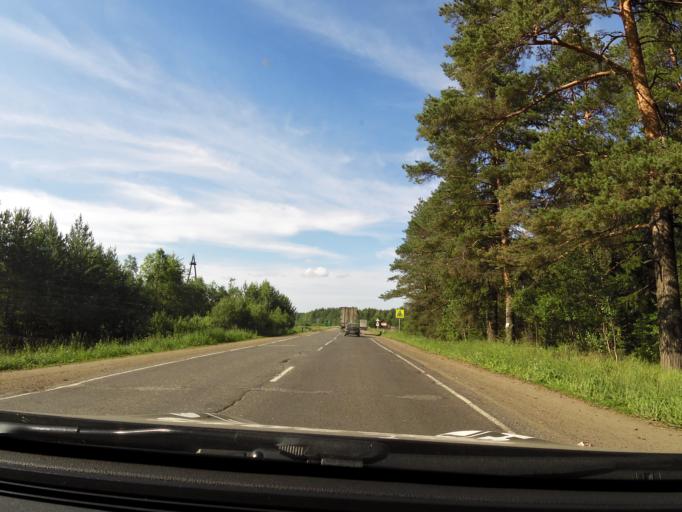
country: RU
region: Kirov
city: Belaya Kholunitsa
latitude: 58.8662
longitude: 50.8428
